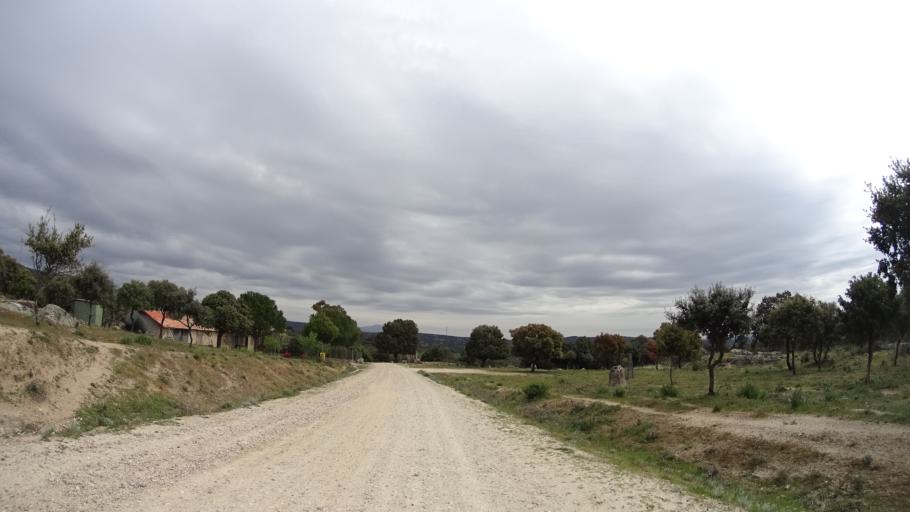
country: ES
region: Madrid
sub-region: Provincia de Madrid
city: Hoyo de Manzanares
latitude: 40.6009
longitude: -3.8810
